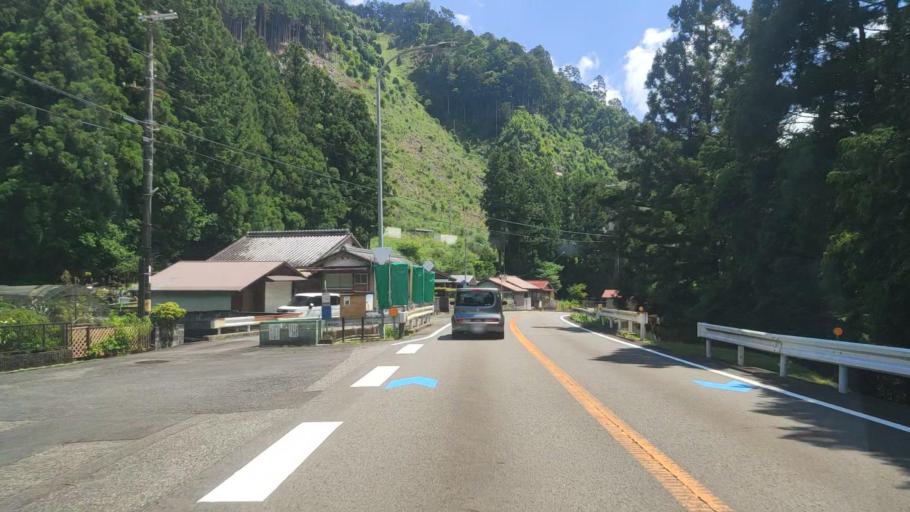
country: JP
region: Mie
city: Owase
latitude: 33.9841
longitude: 136.1083
